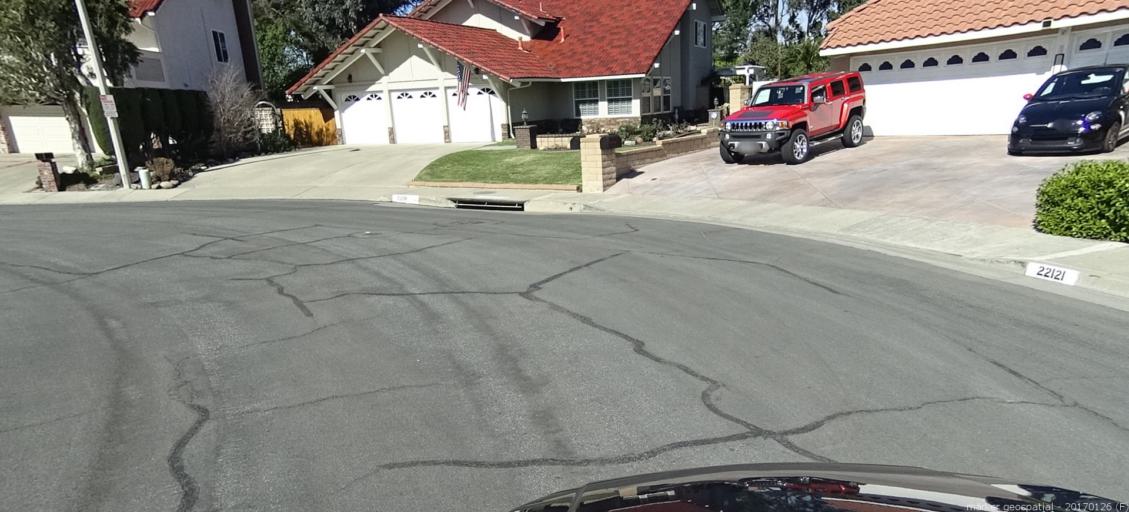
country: US
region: California
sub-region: Orange County
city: Lake Forest
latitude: 33.6410
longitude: -117.6842
